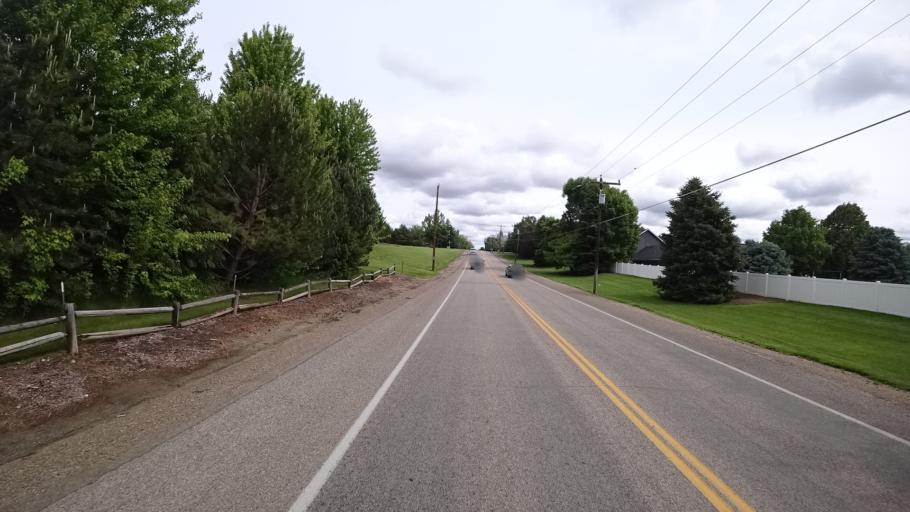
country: US
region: Idaho
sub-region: Ada County
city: Eagle
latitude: 43.7148
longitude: -116.3541
